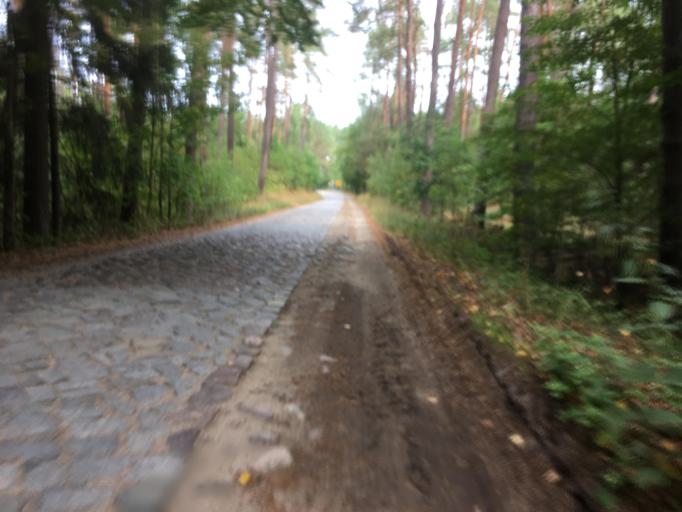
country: DE
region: Brandenburg
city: Milmersdorf
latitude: 53.0587
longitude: 13.6248
